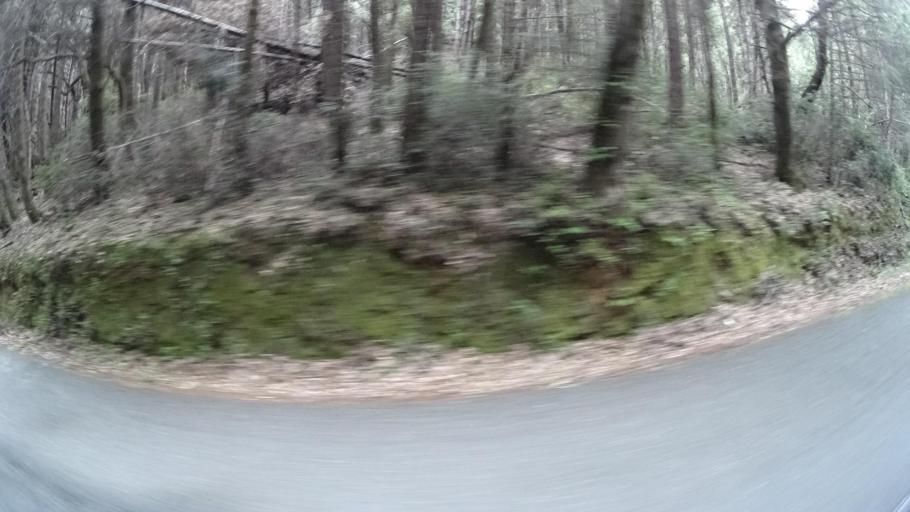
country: US
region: California
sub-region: Humboldt County
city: Willow Creek
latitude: 41.1991
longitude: -123.7593
